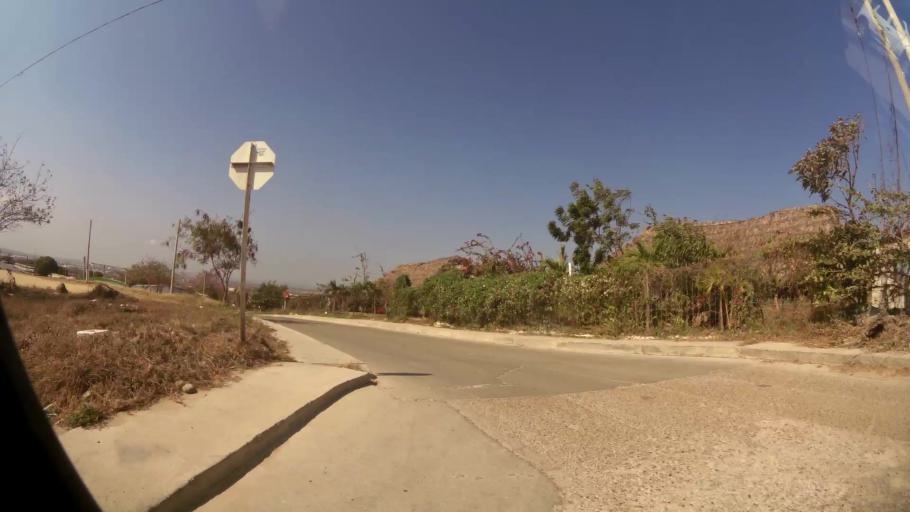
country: CO
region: Atlantico
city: Barranquilla
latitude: 10.9825
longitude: -74.8268
